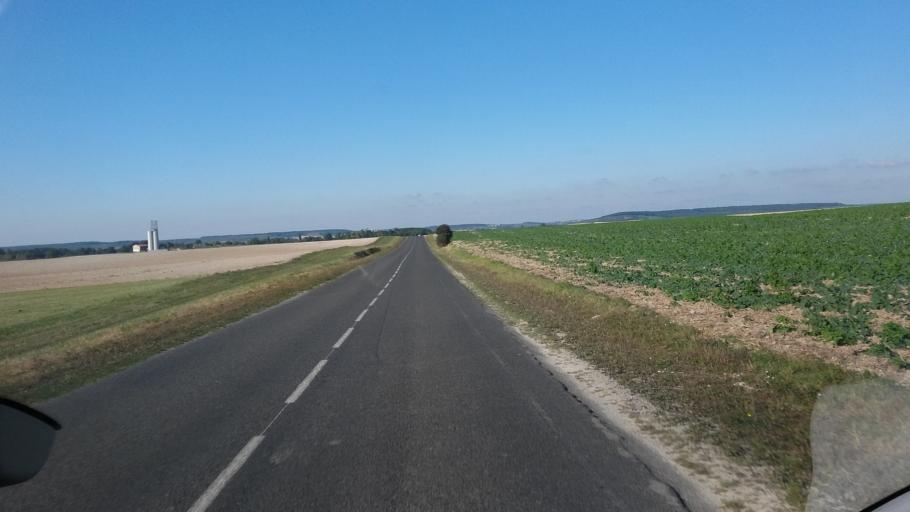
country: FR
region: Champagne-Ardenne
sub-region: Departement de la Marne
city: Connantre
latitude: 48.7736
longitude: 3.8665
